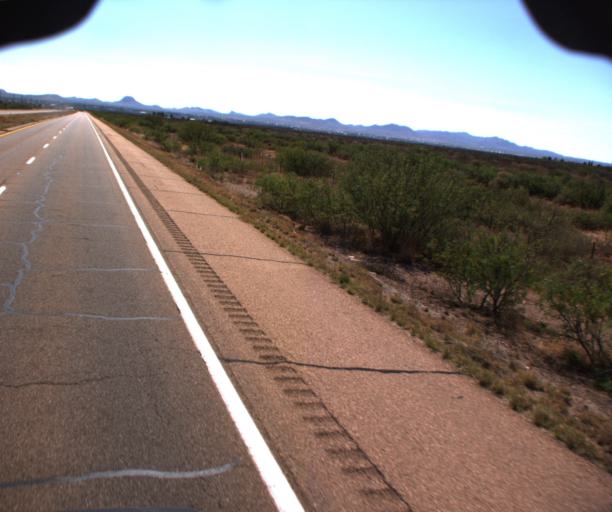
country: US
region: Arizona
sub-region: Cochise County
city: Pirtleville
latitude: 31.3562
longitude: -109.6225
